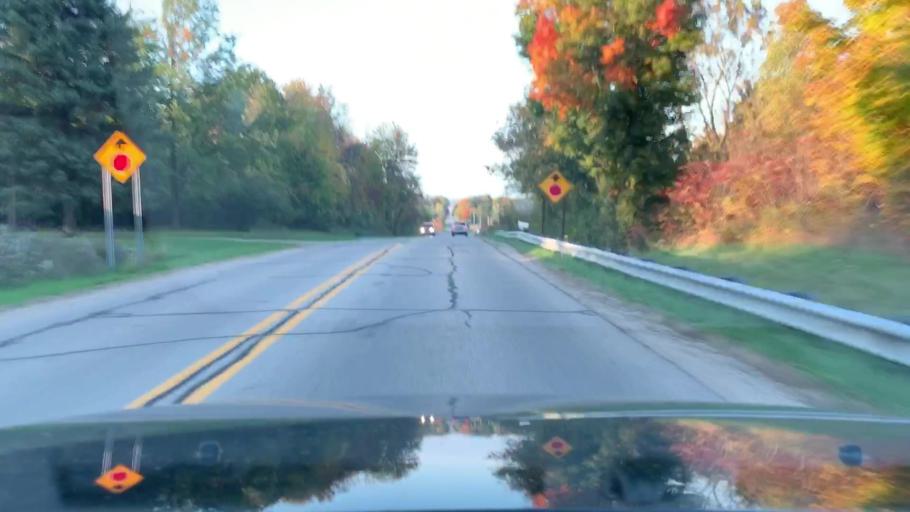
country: US
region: Michigan
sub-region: Ottawa County
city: Hudsonville
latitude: 42.8238
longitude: -85.8025
